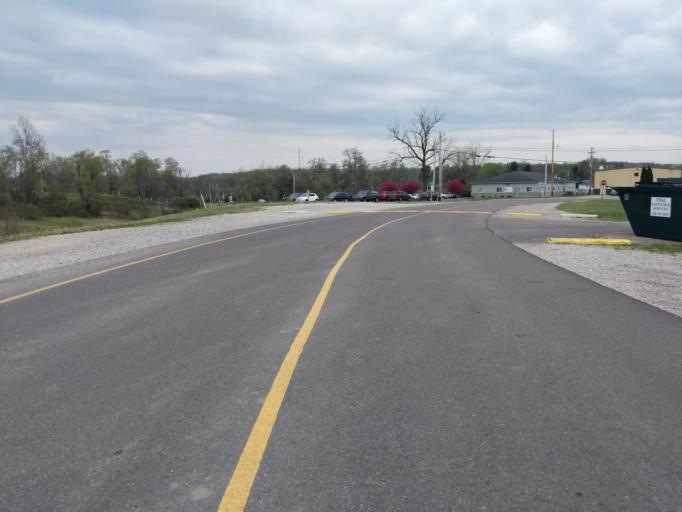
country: US
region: Ohio
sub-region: Athens County
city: The Plains
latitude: 39.3697
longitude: -82.1264
